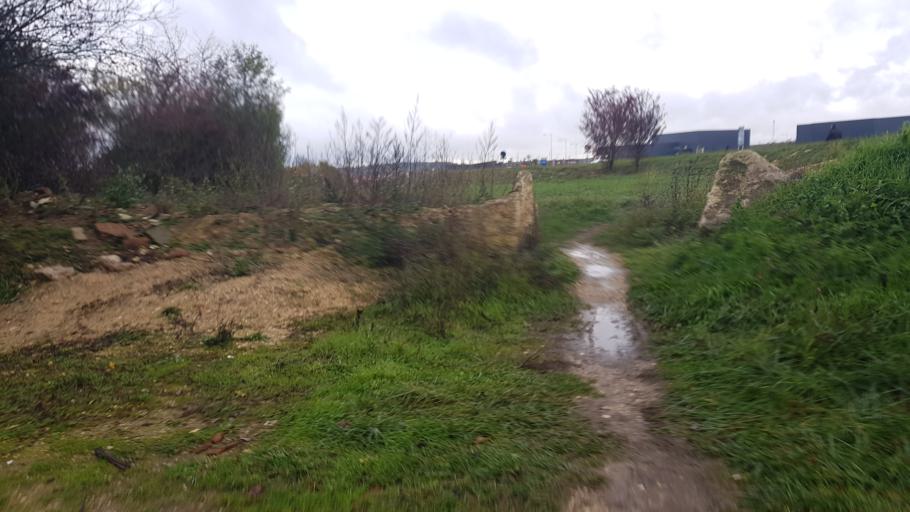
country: FR
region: Poitou-Charentes
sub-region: Departement de la Vienne
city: Chasseneuil-du-Poitou
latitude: 46.6528
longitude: 0.3614
